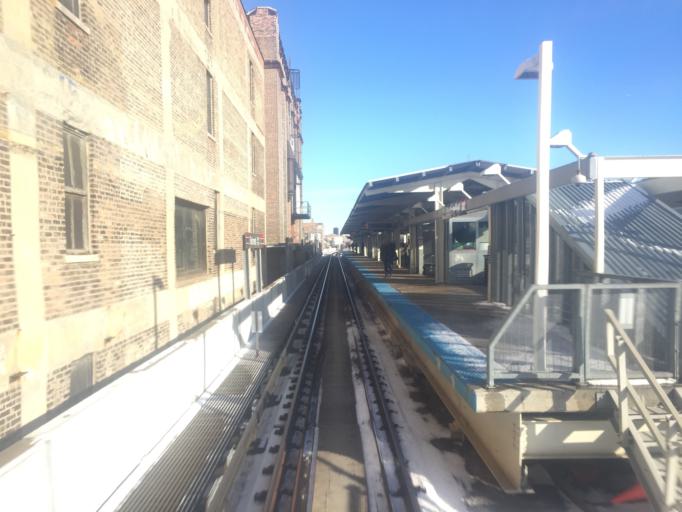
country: US
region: Illinois
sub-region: Cook County
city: Chicago
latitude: 41.9391
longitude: -87.6534
